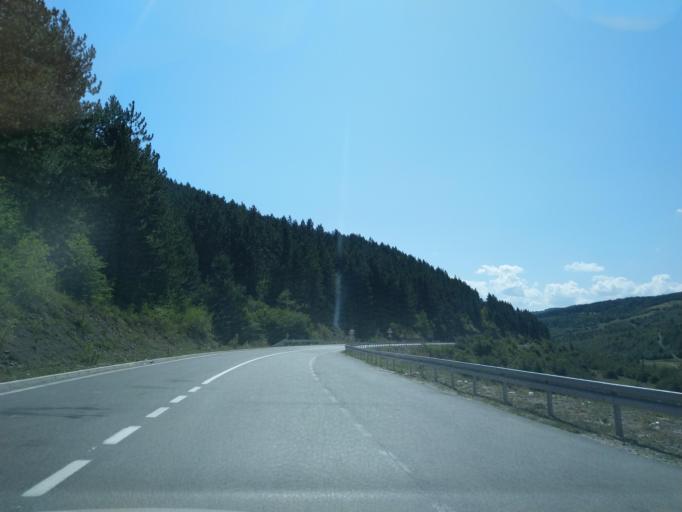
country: RS
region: Central Serbia
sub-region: Zlatiborski Okrug
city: Sjenica
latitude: 43.2928
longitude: 19.9403
